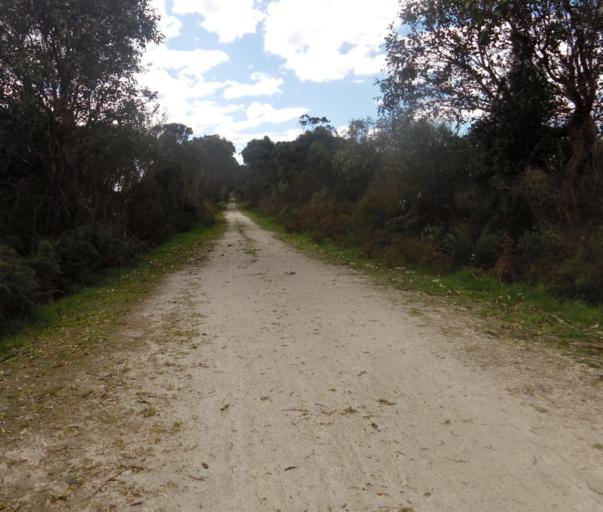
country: AU
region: Victoria
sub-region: Bass Coast
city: North Wonthaggi
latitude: -38.6204
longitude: 146.0406
